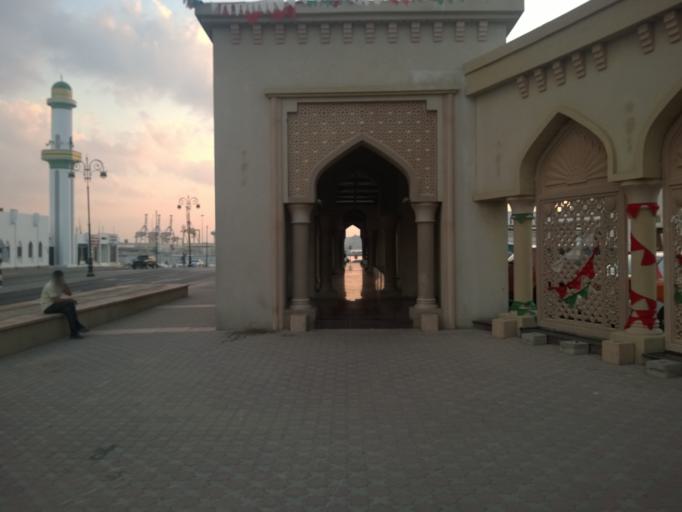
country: OM
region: Muhafazat Masqat
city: Muscat
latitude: 23.6233
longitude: 58.5605
